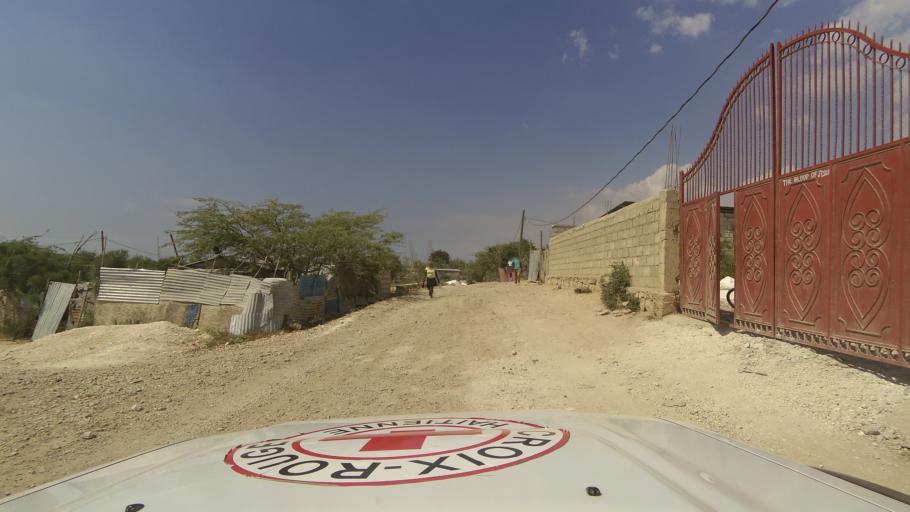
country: HT
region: Ouest
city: Croix des Bouquets
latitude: 18.6481
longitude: -72.2630
